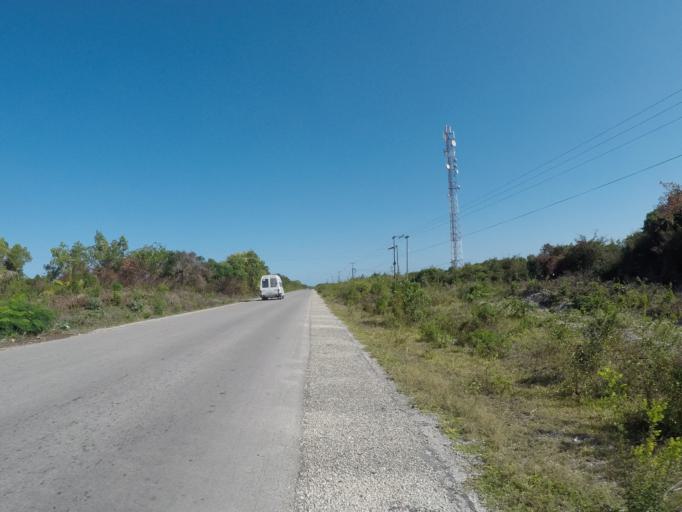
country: TZ
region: Zanzibar Central/South
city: Nganane
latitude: -6.1775
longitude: 39.5272
